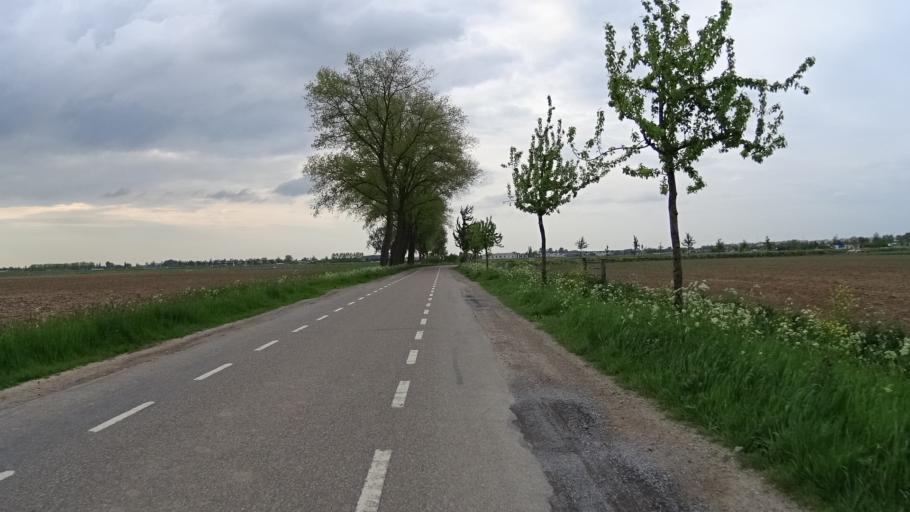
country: NL
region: North Brabant
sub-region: Gemeente Aalburg
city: Aalburg
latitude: 51.7624
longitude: 5.0990
